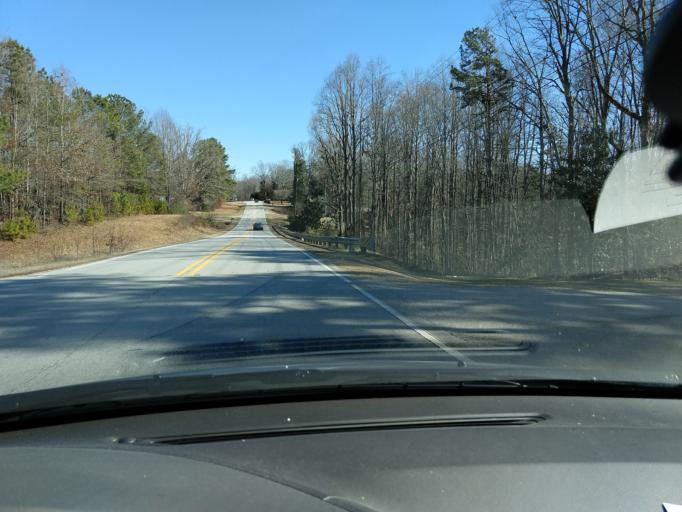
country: US
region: Georgia
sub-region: Stephens County
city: Toccoa
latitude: 34.6147
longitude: -83.4087
